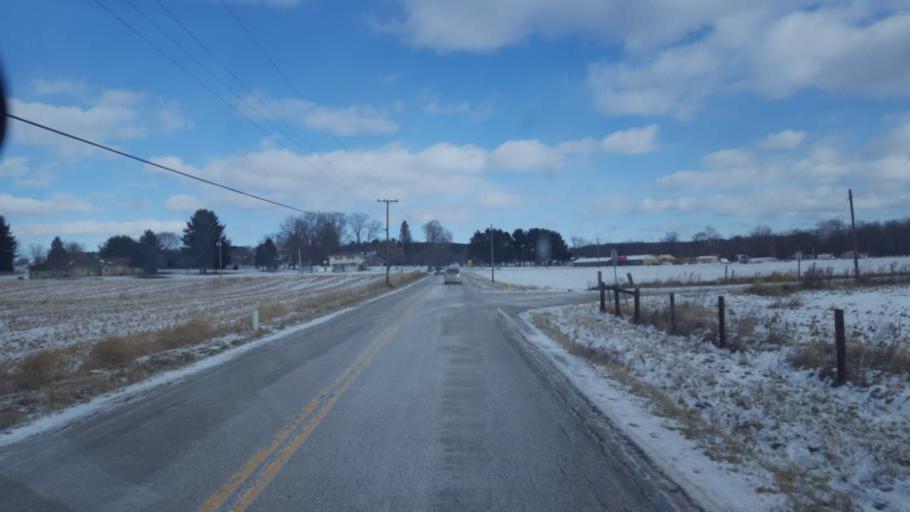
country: US
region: Ohio
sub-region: Coshocton County
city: Coshocton
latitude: 40.3085
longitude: -81.8272
